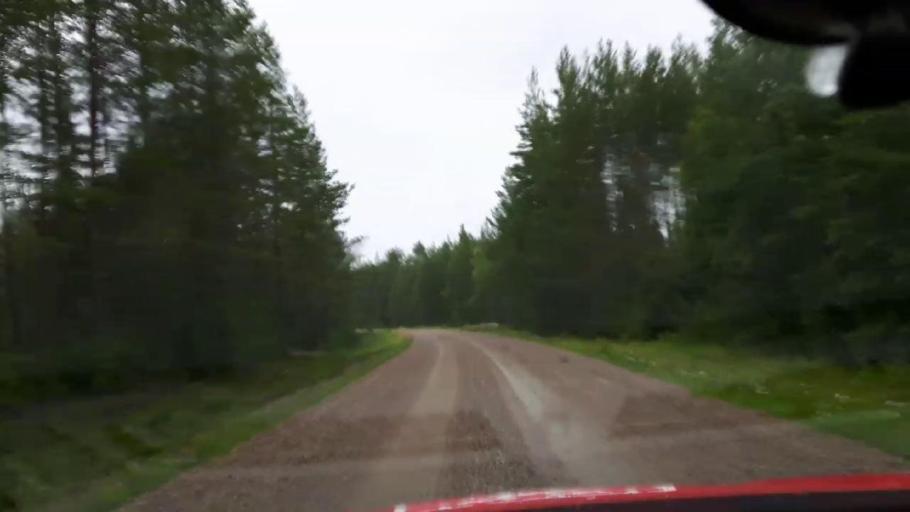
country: SE
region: Jaemtland
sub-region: OEstersunds Kommun
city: Brunflo
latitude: 62.8073
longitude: 14.8959
